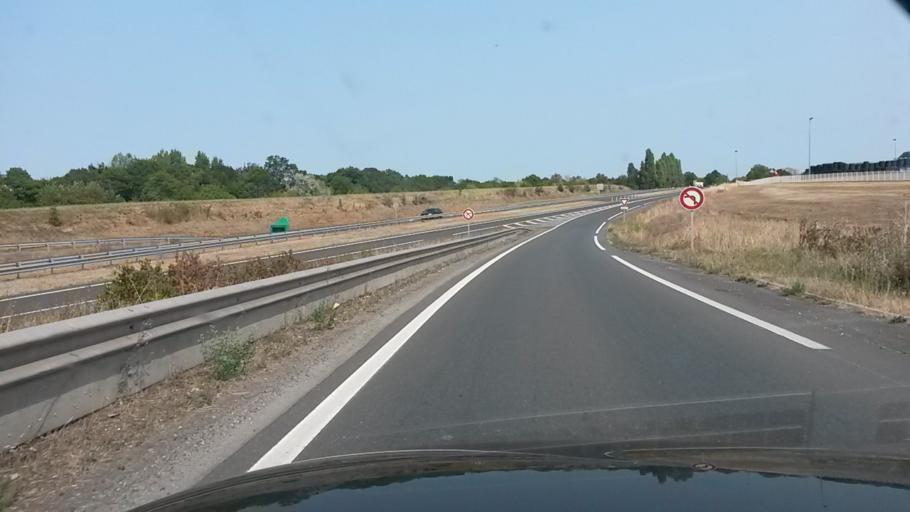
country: FR
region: Pays de la Loire
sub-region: Departement de la Loire-Atlantique
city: Saint-Gereon
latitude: 47.3908
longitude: -1.1873
